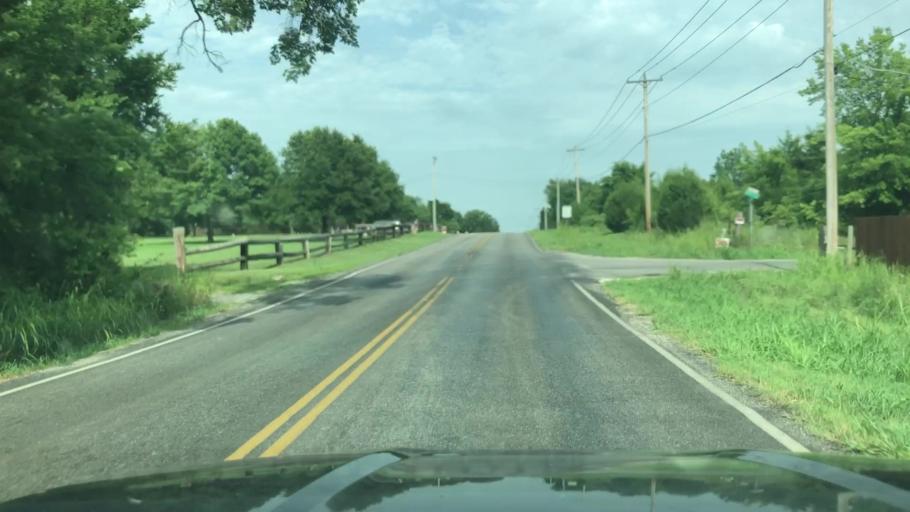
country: US
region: Oklahoma
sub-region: Tulsa County
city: Oakhurst
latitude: 36.0902
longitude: -96.1013
